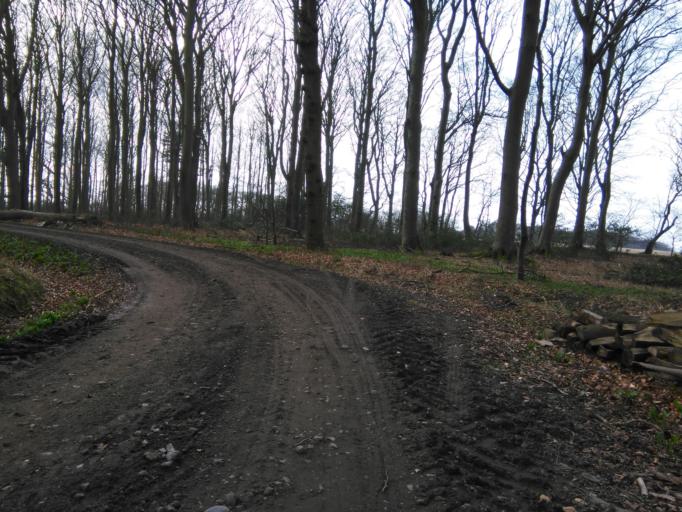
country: DK
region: Central Jutland
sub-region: Odder Kommune
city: Odder
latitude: 55.8465
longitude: 10.1658
